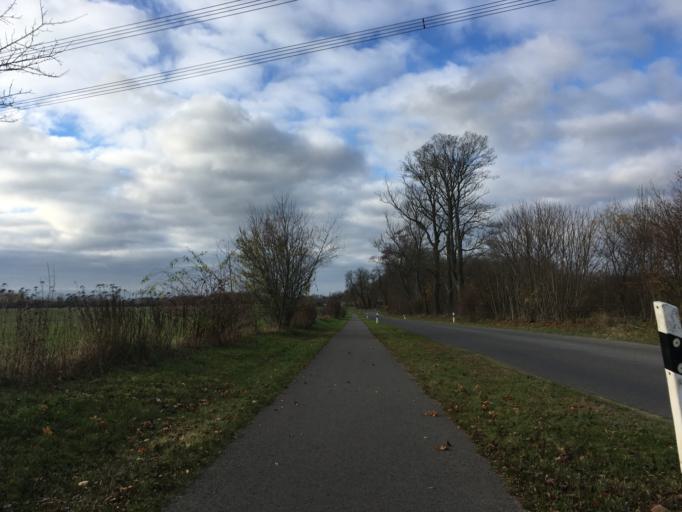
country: DE
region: Brandenburg
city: Rehfelde
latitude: 52.5323
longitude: 13.9561
